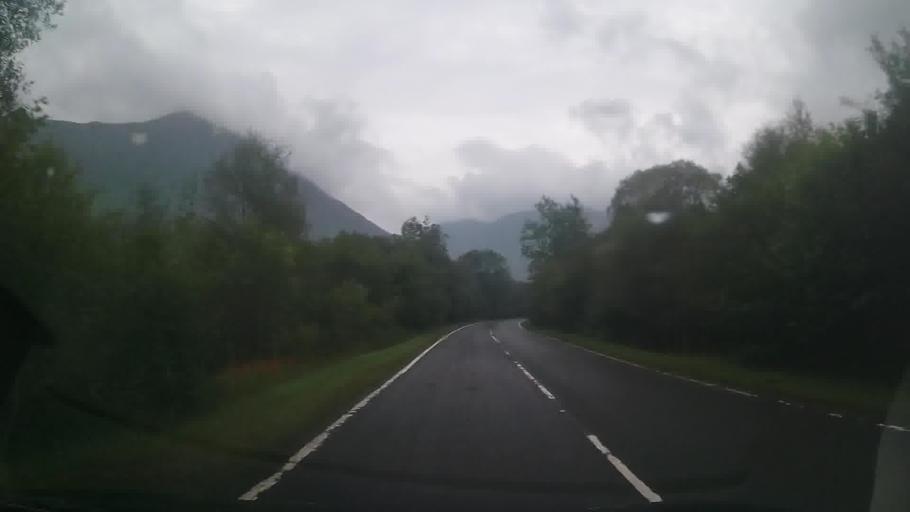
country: GB
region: Scotland
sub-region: Highland
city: Fort William
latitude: 56.6747
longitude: -5.0856
